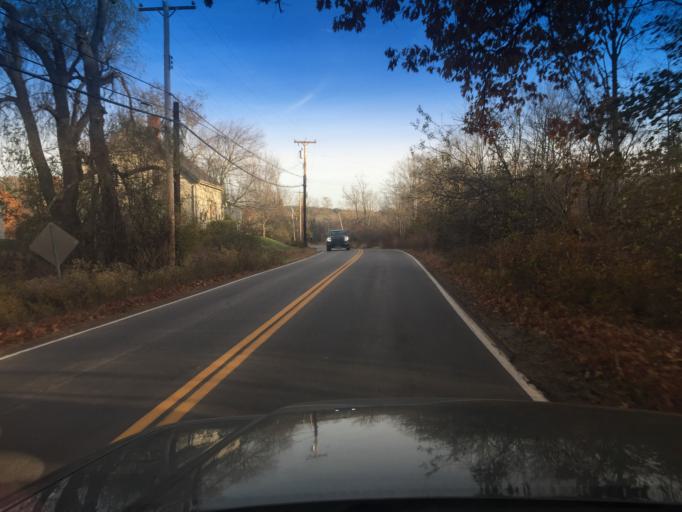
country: US
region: Maine
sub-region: York County
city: Eliot
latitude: 43.1786
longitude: -70.7281
